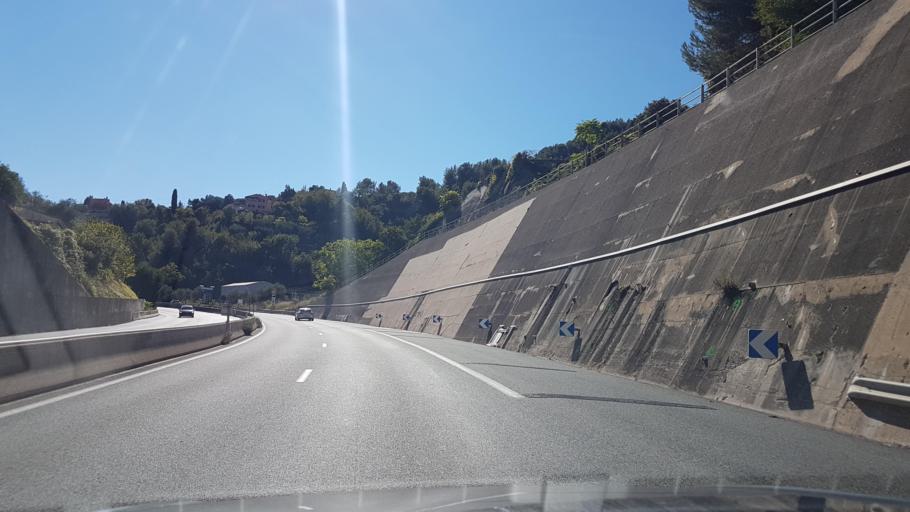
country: FR
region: Provence-Alpes-Cote d'Azur
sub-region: Departement des Alpes-Maritimes
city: Sainte-Agnes
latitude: 43.7959
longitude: 7.4775
